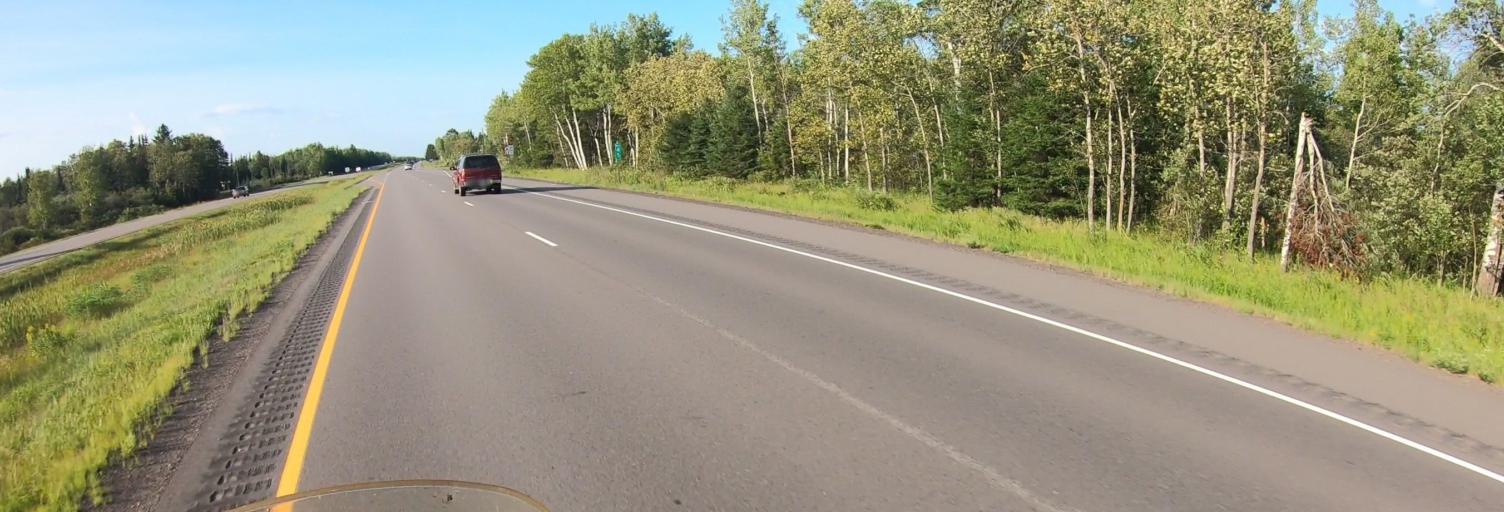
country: US
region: Minnesota
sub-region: Saint Louis County
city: Eveleth
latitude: 47.2541
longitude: -92.4820
